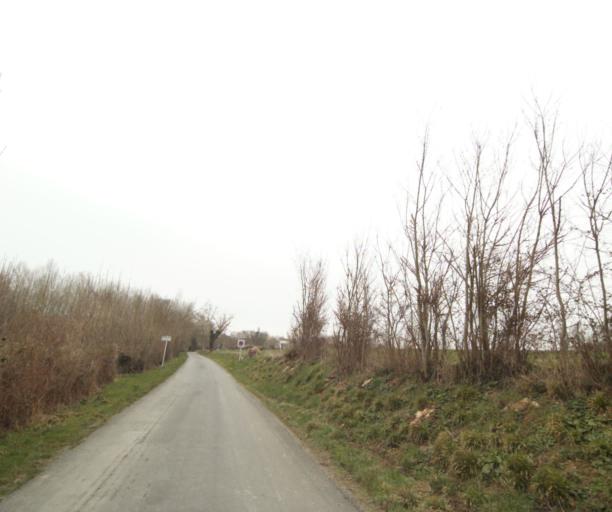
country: FR
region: Poitou-Charentes
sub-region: Departement des Deux-Sevres
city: Magne
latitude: 46.3203
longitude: -0.5328
